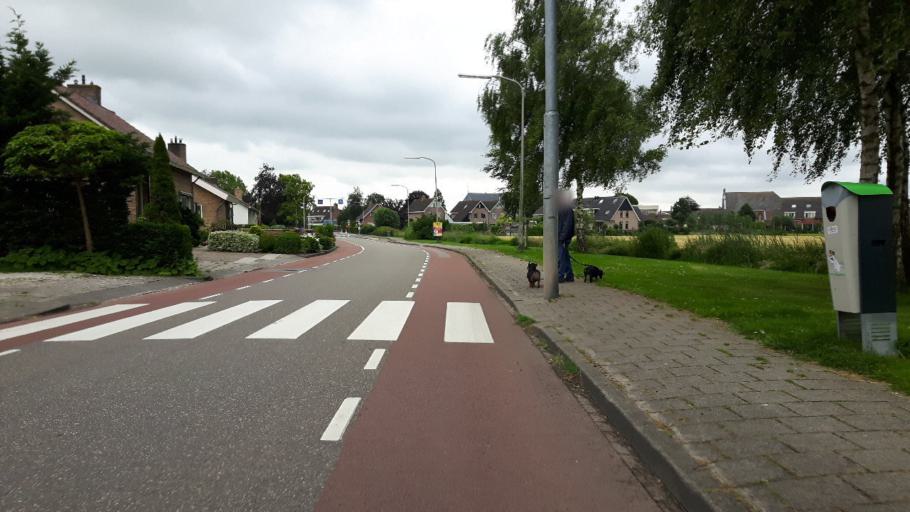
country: NL
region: Utrecht
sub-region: Gemeente Oudewater
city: Oudewater
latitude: 52.0632
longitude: 4.8210
